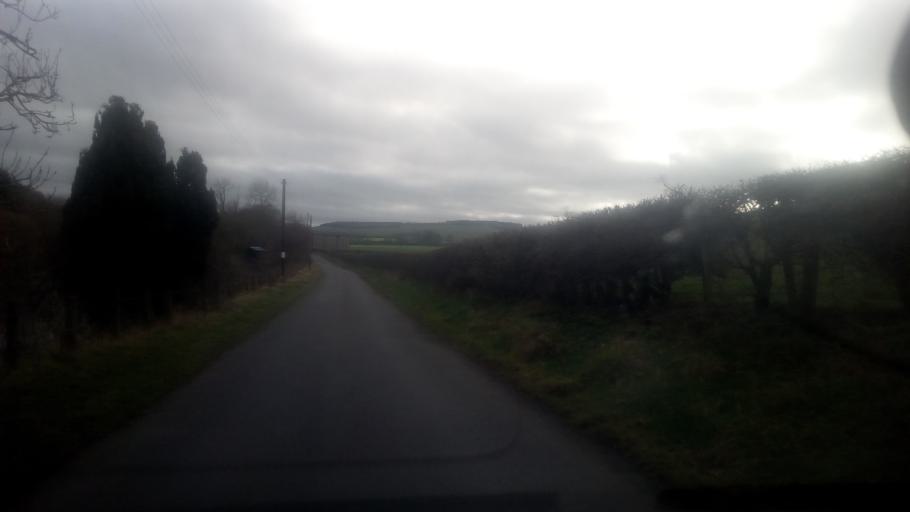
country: GB
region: Scotland
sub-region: The Scottish Borders
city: Kelso
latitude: 55.5461
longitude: -2.4753
